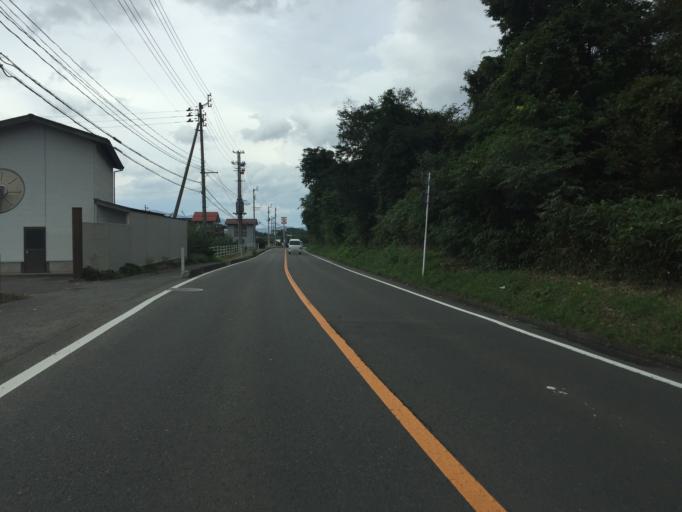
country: JP
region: Fukushima
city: Hobaramachi
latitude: 37.8001
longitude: 140.5172
